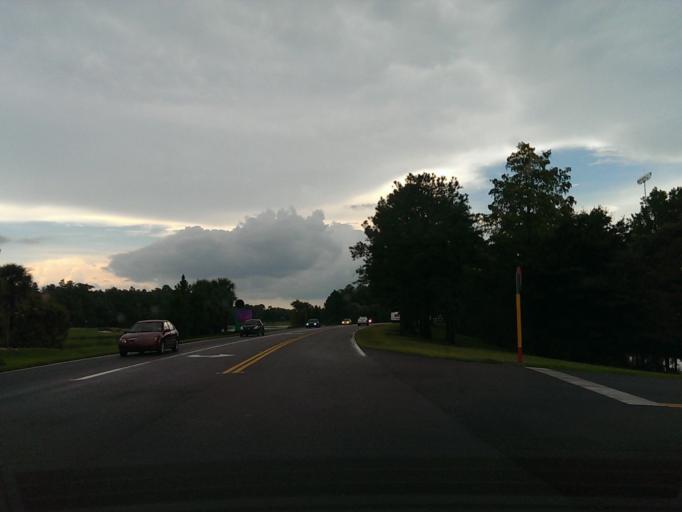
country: US
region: Florida
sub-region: Polk County
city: Citrus Ridge
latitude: 28.3989
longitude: -81.5840
